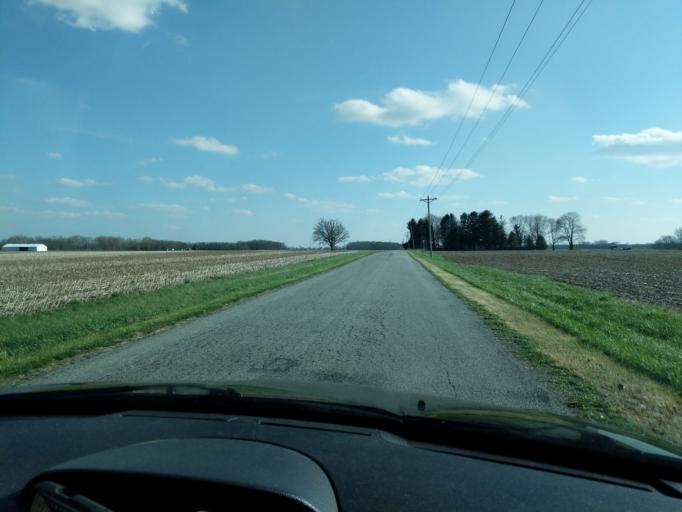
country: US
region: Ohio
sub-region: Champaign County
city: Urbana
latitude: 40.1426
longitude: -83.8154
